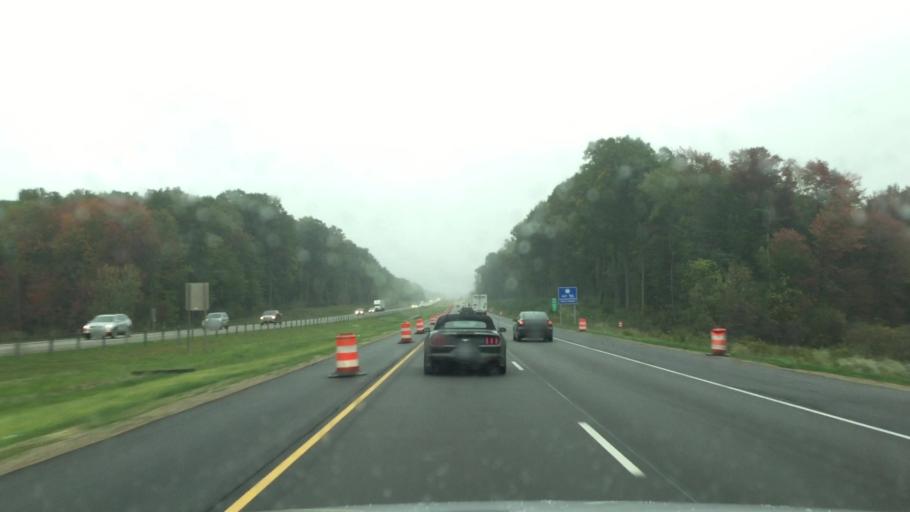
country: US
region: Michigan
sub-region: Van Buren County
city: Decatur
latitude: 42.1931
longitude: -85.9872
